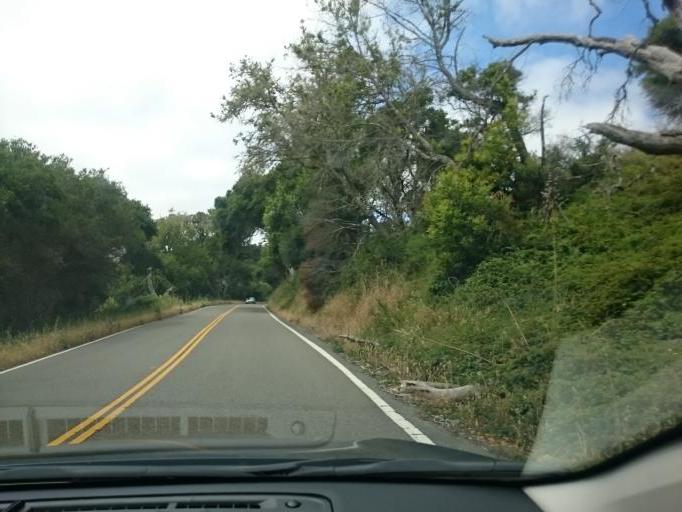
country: US
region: California
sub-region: Marin County
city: Bolinas
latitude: 37.9496
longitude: -122.7119
